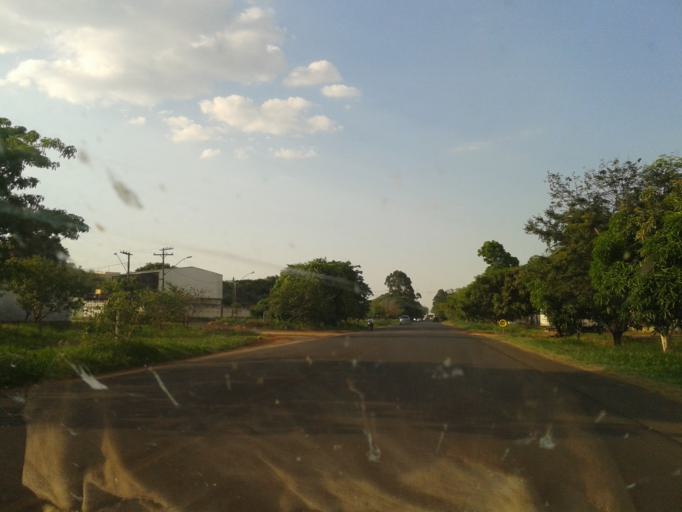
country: BR
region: Minas Gerais
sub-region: Uberlandia
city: Uberlandia
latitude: -18.9482
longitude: -48.3070
